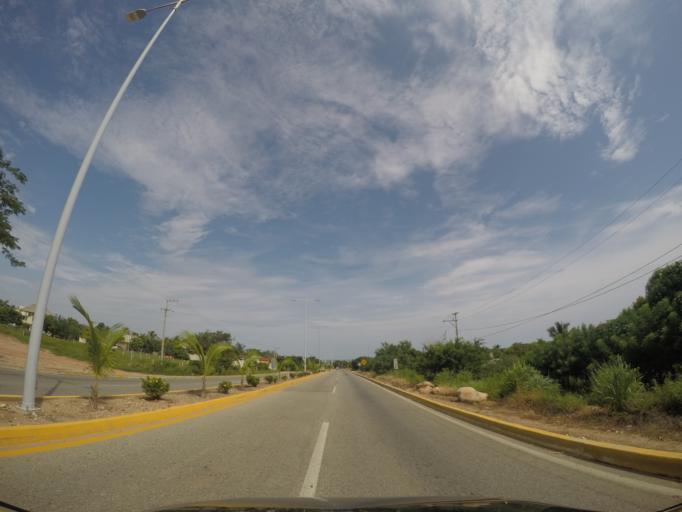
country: MX
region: Oaxaca
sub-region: Santa Maria Colotepec
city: Brisas de Zicatela
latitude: 15.8295
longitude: -97.0323
